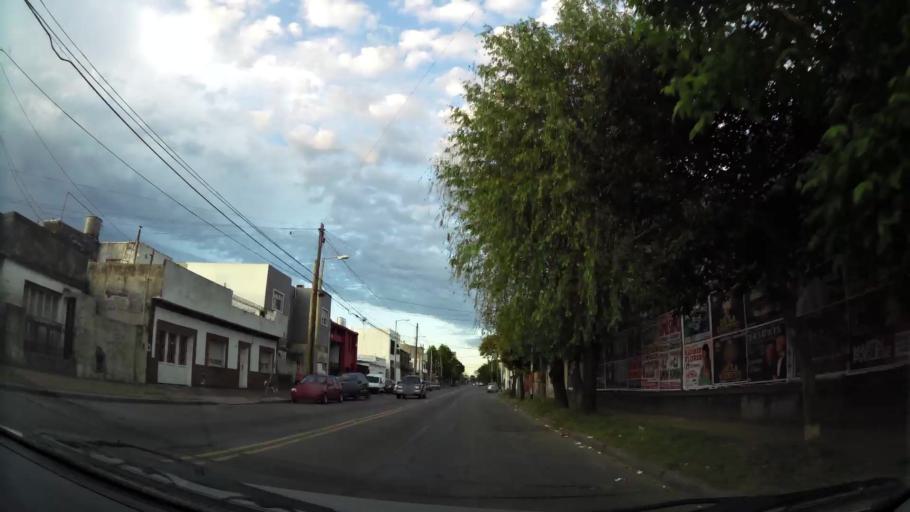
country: AR
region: Buenos Aires
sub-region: Partido de Avellaneda
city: Avellaneda
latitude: -34.7024
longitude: -58.3326
